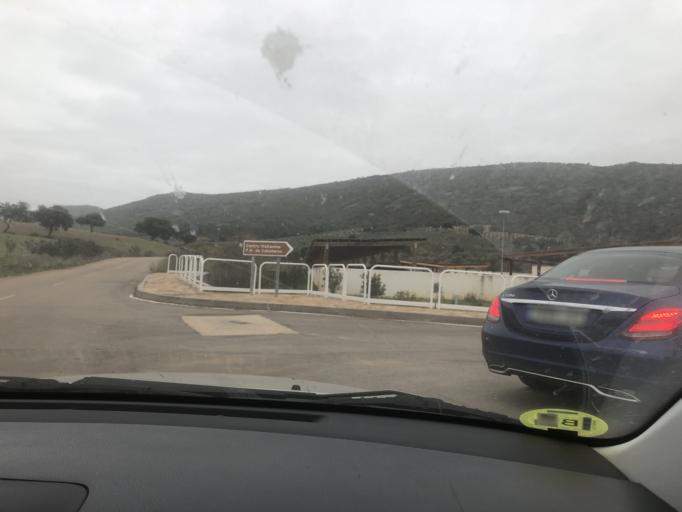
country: ES
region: Castille-La Mancha
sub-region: Provincia de Ciudad Real
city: Navalpino
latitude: 39.3247
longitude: -4.6254
